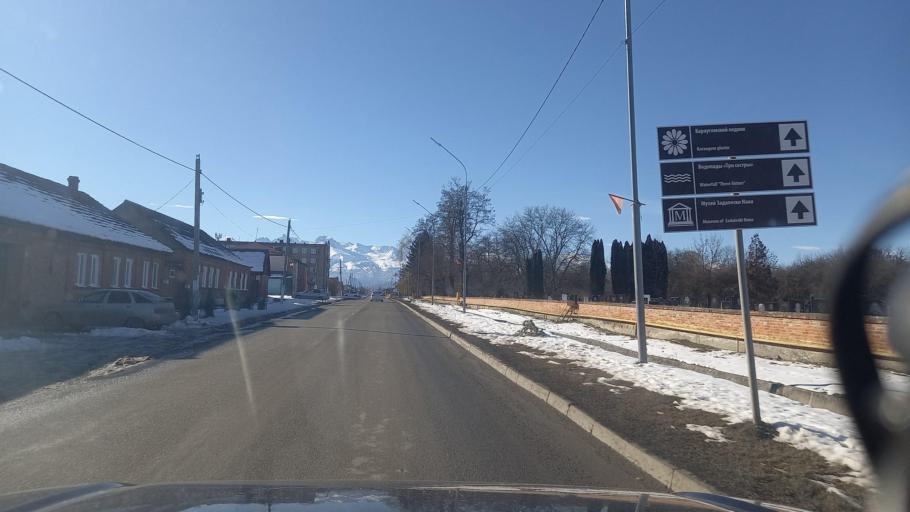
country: RU
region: North Ossetia
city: Chikola
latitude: 43.1989
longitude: 43.9227
